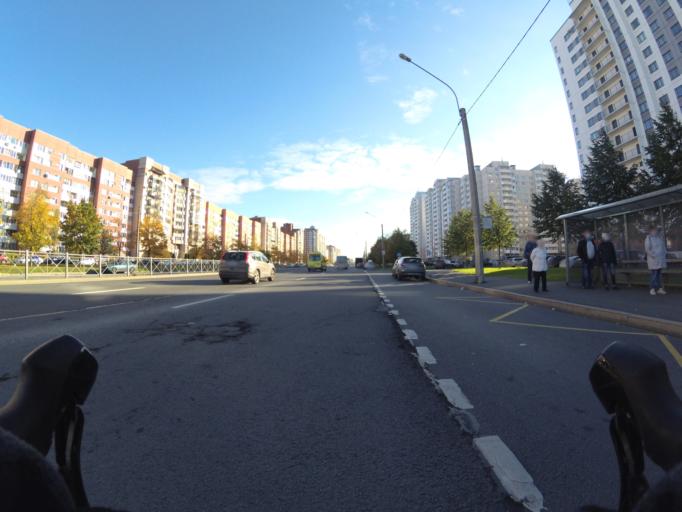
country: RU
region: Leningrad
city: Untolovo
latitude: 60.0080
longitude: 30.2037
